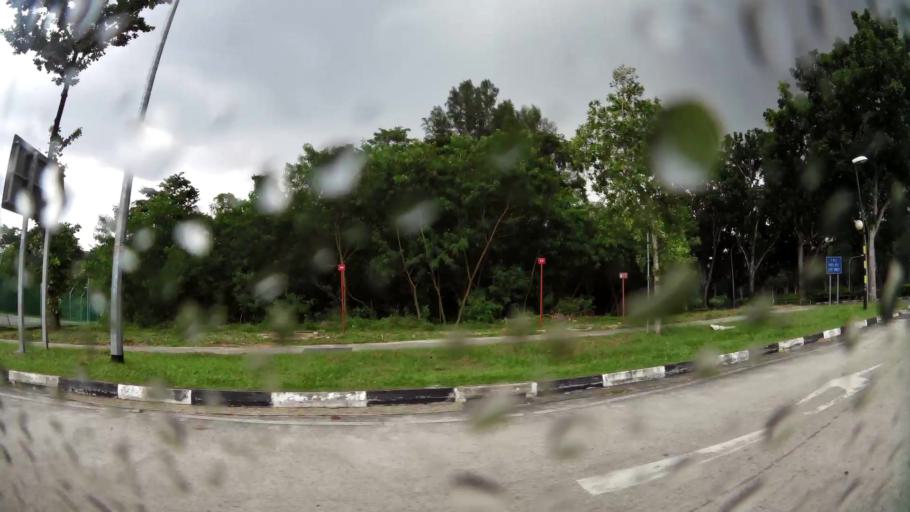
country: MY
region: Johor
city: Kampung Pasir Gudang Baru
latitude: 1.4019
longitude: 103.8724
